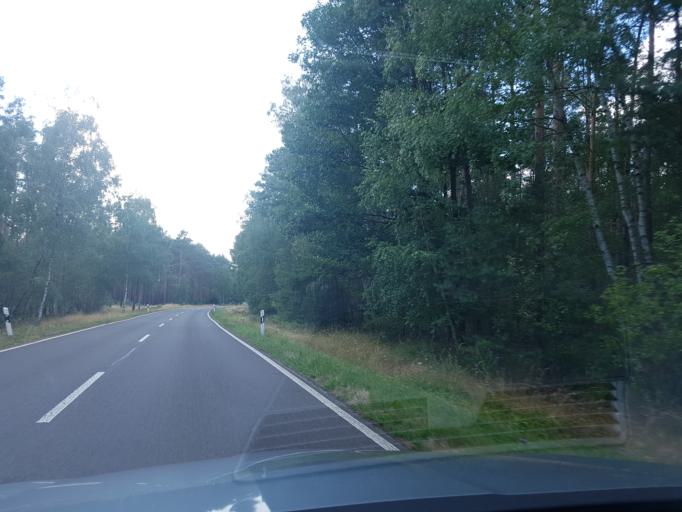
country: DE
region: Brandenburg
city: Schlieben
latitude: 51.6834
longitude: 13.4563
